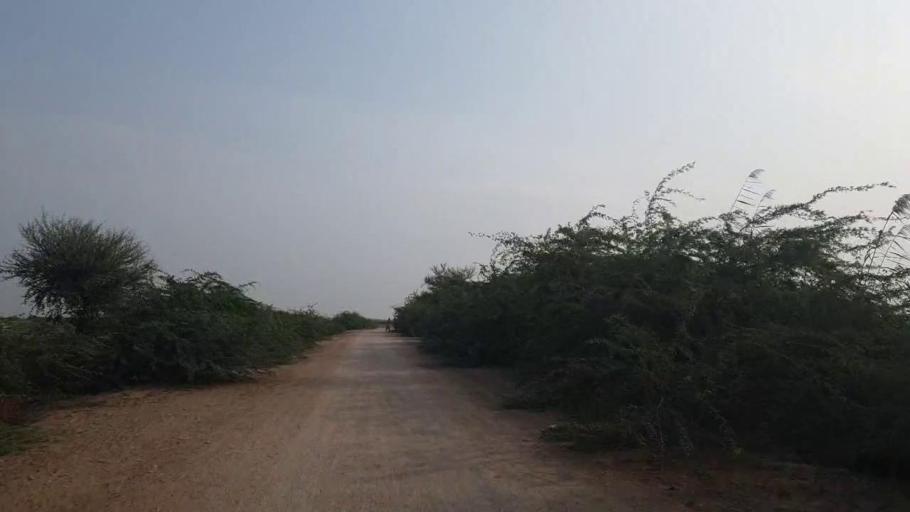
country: PK
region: Sindh
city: Badin
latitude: 24.6080
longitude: 68.6881
